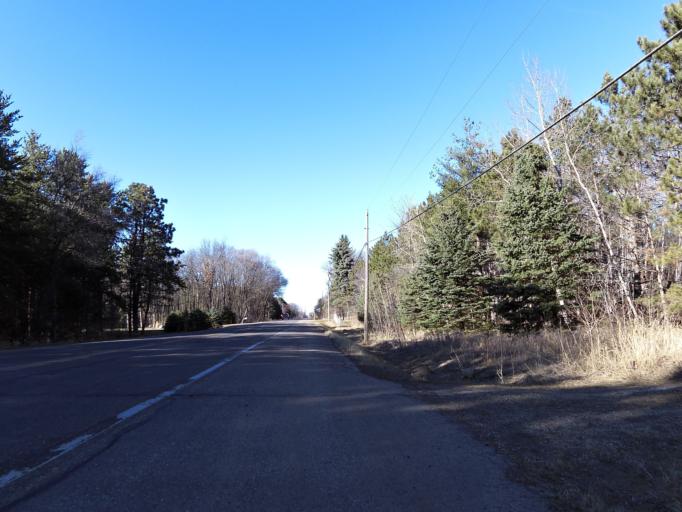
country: US
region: Minnesota
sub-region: Washington County
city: Bayport
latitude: 44.9835
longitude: -92.8224
